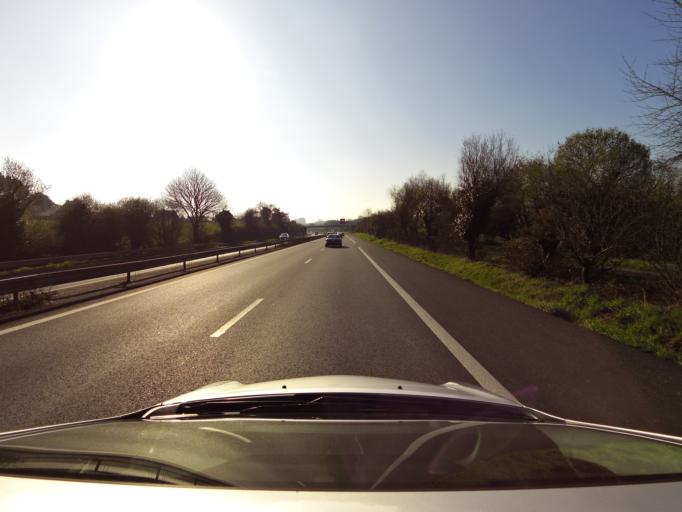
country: FR
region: Brittany
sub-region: Departement du Morbihan
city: Queven
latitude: 47.7747
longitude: -3.3918
